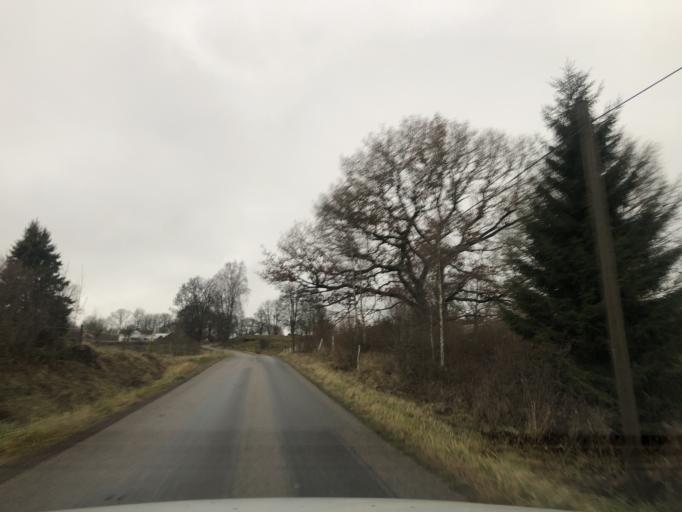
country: SE
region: Vaestra Goetaland
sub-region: Ulricehamns Kommun
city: Ulricehamn
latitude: 57.8884
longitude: 13.4287
